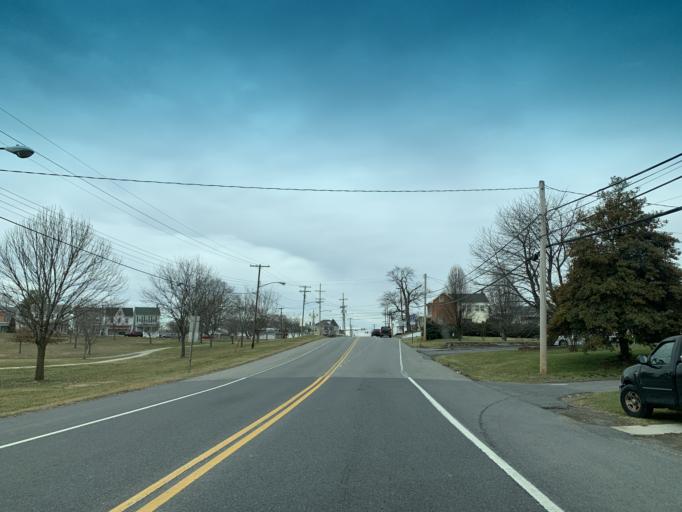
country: US
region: Maryland
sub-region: Washington County
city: Hagerstown
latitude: 39.6221
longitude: -77.7287
